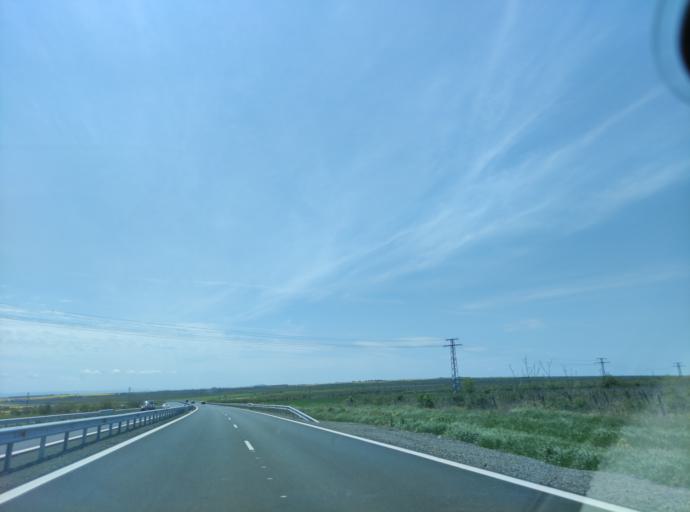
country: BG
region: Burgas
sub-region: Obshtina Pomorie
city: Pomorie
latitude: 42.5827
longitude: 27.5842
